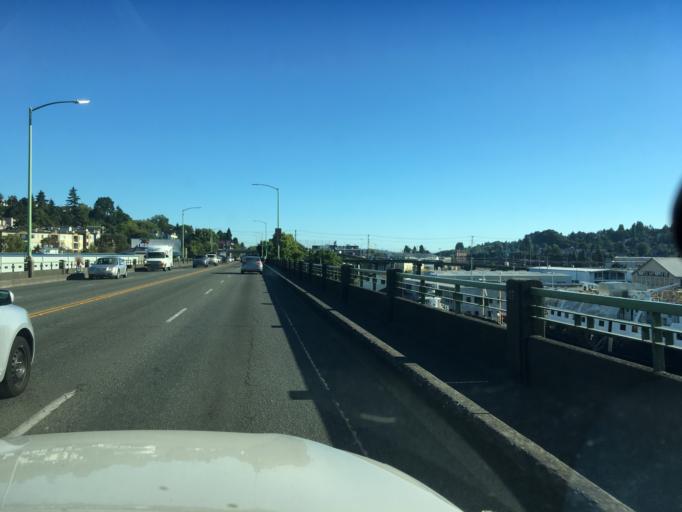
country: US
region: Washington
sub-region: King County
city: Seattle
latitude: 47.6570
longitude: -122.3763
